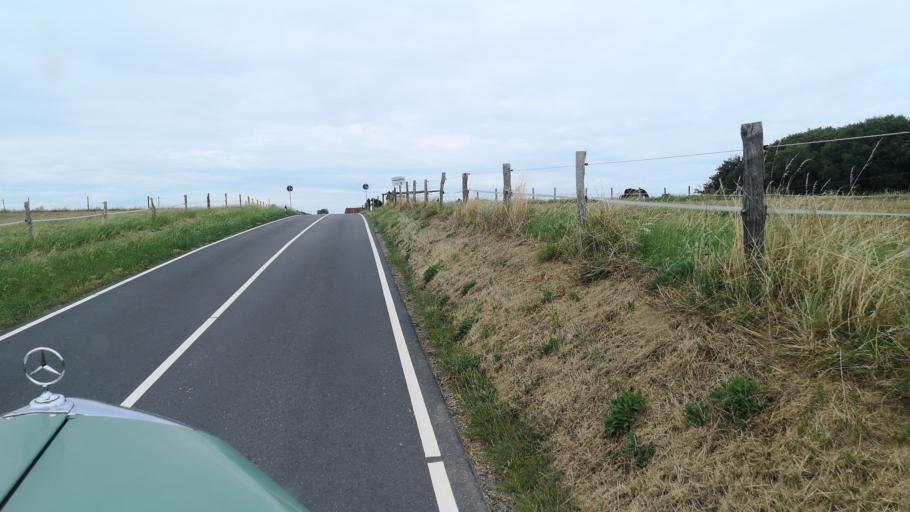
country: DE
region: North Rhine-Westphalia
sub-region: Regierungsbezirk Koln
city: Odenthal
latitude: 51.0506
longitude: 7.1850
